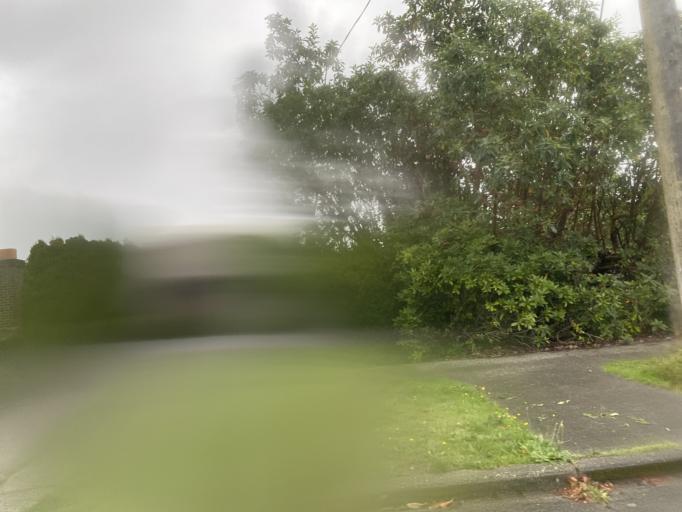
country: US
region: Washington
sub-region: King County
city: Seattle
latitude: 47.6506
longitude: -122.4047
